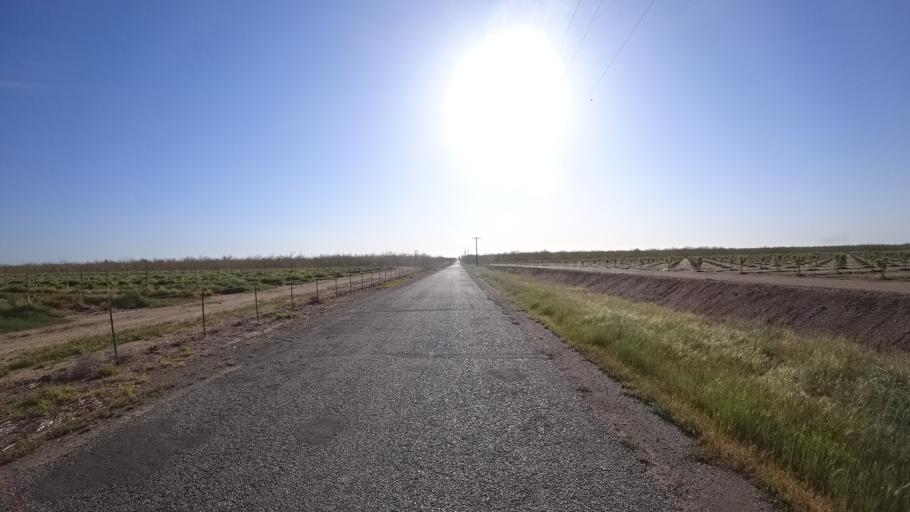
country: US
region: California
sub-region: Glenn County
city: Orland
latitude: 39.6821
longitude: -122.1737
